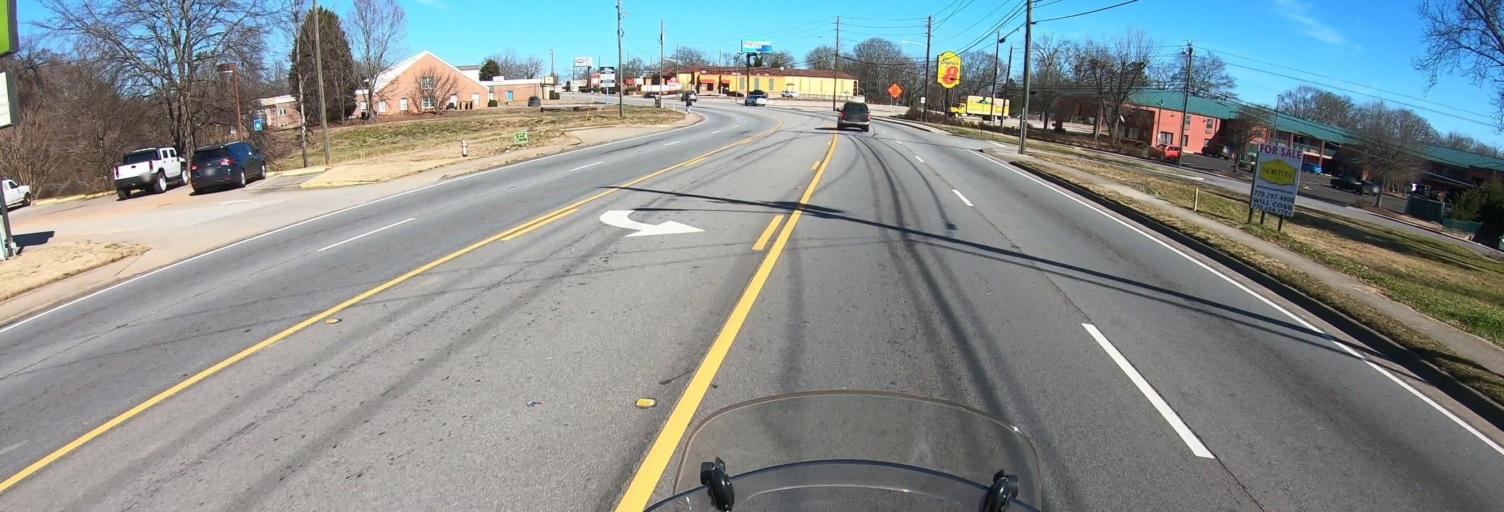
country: US
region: Georgia
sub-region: Hall County
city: Gainesville
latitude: 34.2899
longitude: -83.8331
